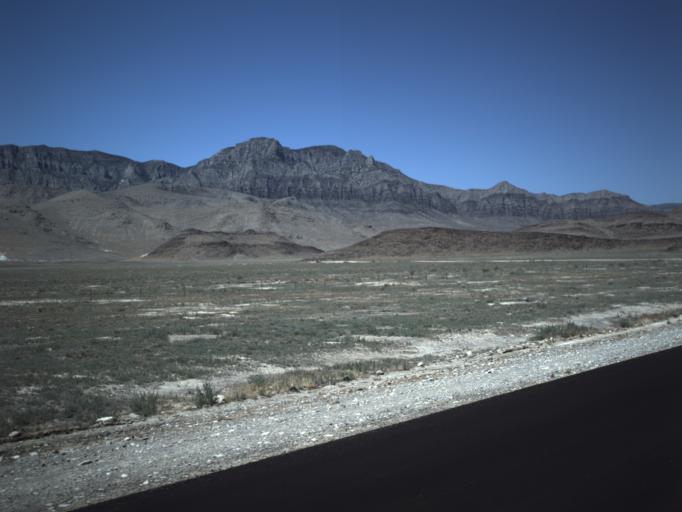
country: US
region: Utah
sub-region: Beaver County
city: Milford
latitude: 39.0516
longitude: -113.4214
